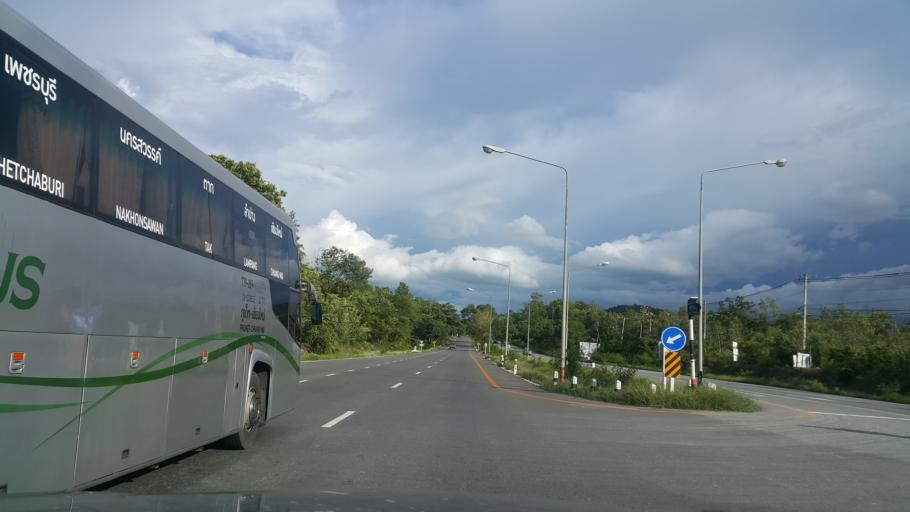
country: TH
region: Tak
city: Ban Tak
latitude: 16.9791
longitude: 99.1237
